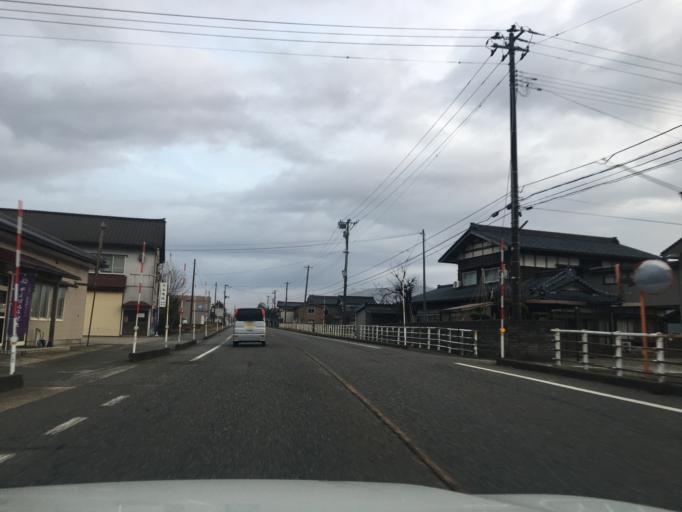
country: JP
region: Niigata
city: Murakami
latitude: 38.3241
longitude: 139.5557
